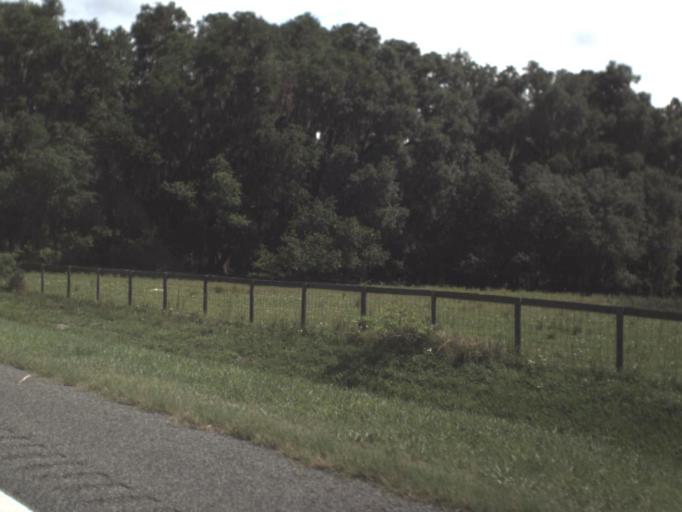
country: US
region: Florida
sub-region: Alachua County
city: Gainesville
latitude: 29.5978
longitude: -82.3392
